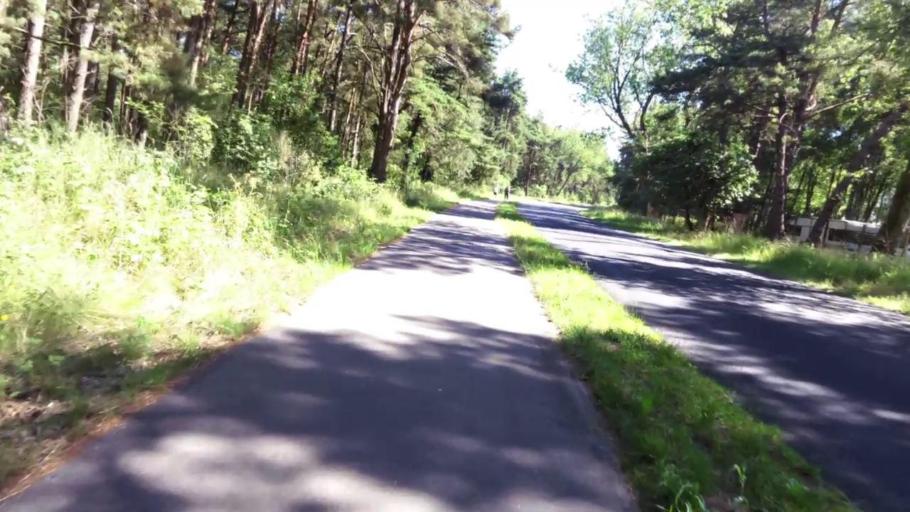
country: PL
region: West Pomeranian Voivodeship
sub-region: Koszalin
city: Koszalin
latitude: 54.2952
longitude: 16.1699
